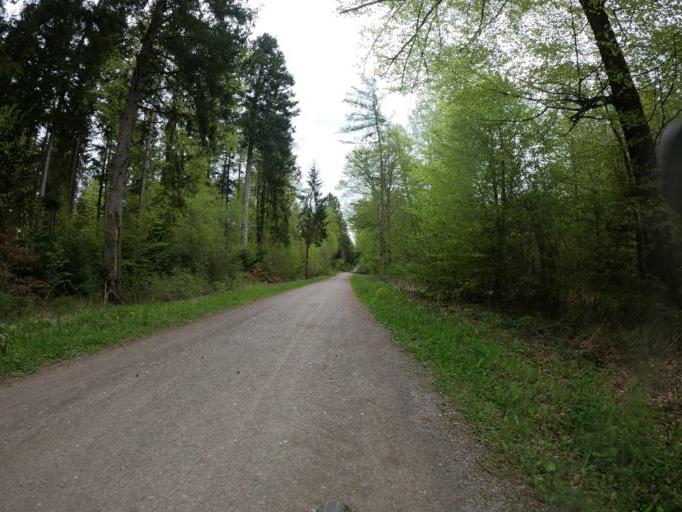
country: DE
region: Baden-Wuerttemberg
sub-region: Karlsruhe Region
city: Rohrdorf
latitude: 48.5501
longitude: 8.6903
